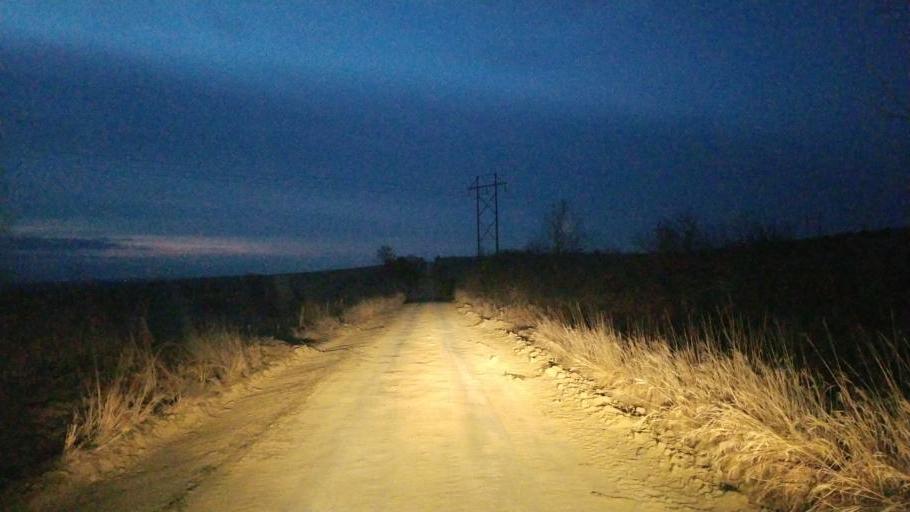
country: US
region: Nebraska
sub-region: Knox County
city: Center
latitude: 42.5709
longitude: -97.7984
